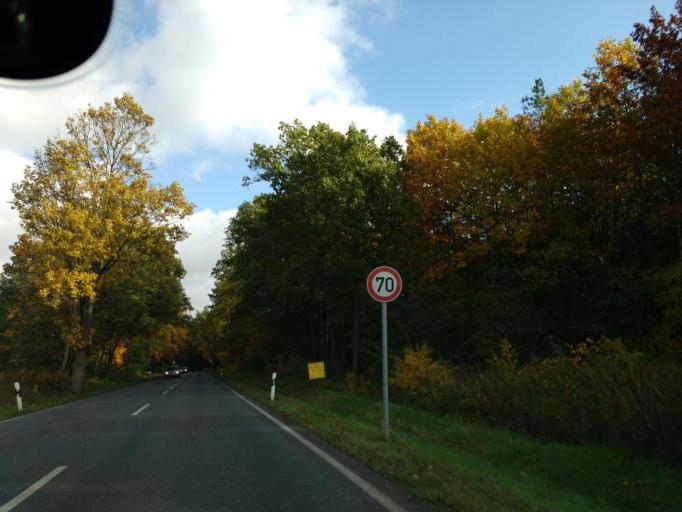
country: DE
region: Brandenburg
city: Petershagen
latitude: 52.5582
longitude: 13.8157
